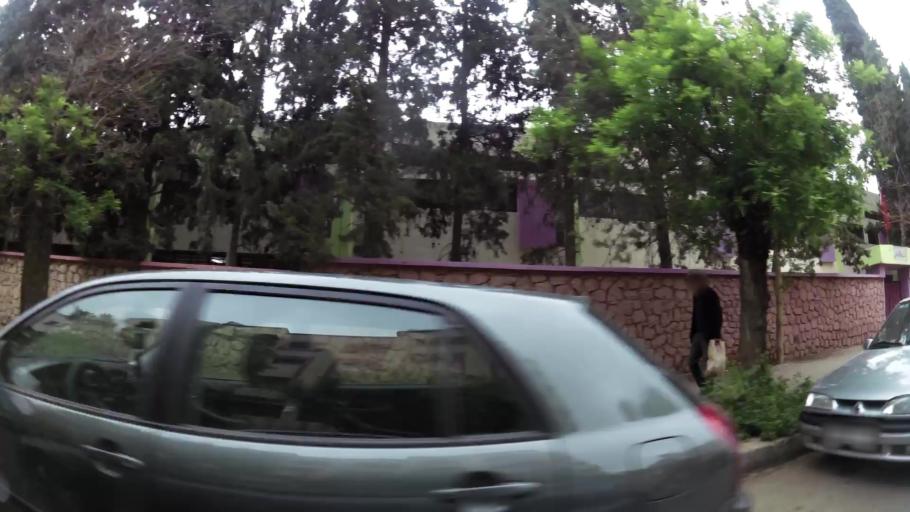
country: MA
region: Fes-Boulemane
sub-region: Fes
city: Fes
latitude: 34.0419
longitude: -5.0083
